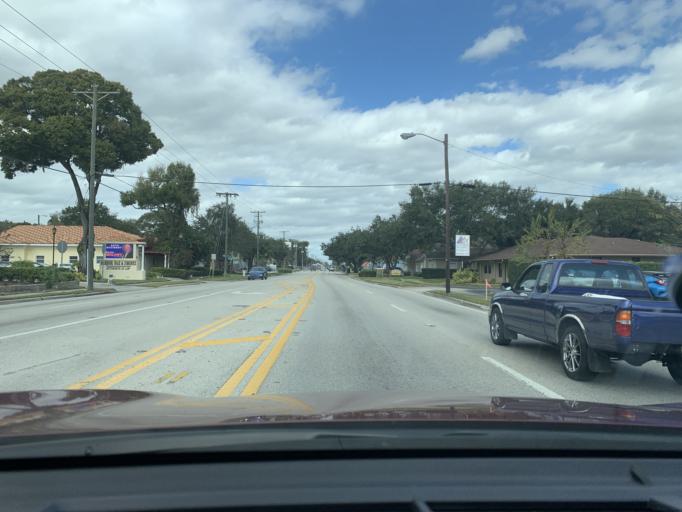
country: US
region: Florida
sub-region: Hillsborough County
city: Egypt Lake-Leto
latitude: 27.9832
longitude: -82.4846
